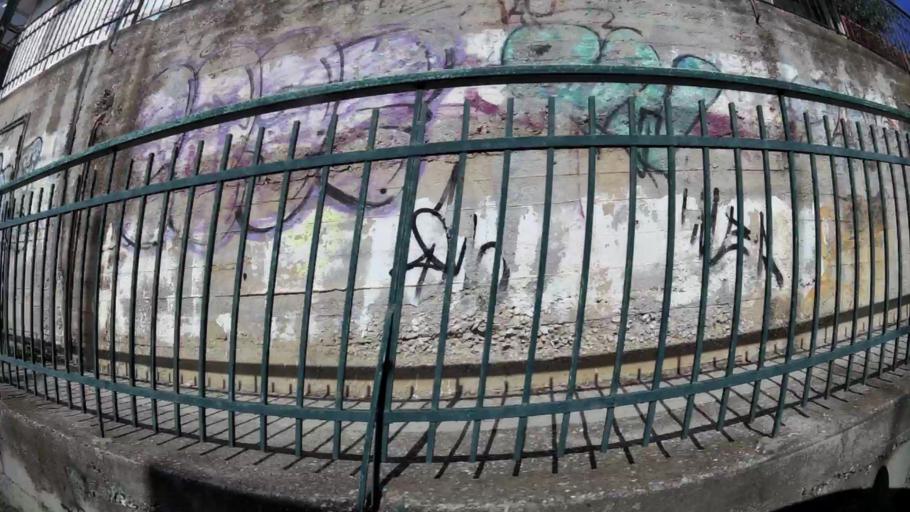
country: GR
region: Attica
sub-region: Nomos Piraios
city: Keratsini
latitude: 37.9613
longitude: 23.6148
